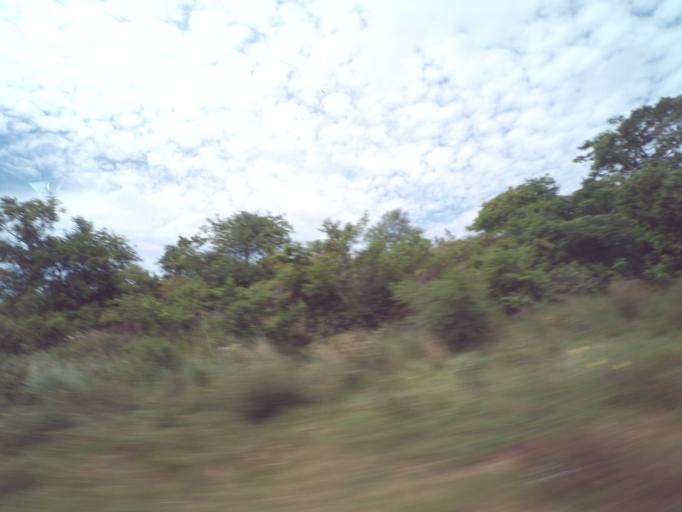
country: BO
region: Santa Cruz
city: Santa Cruz de la Sierra
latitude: -17.9170
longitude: -63.1609
